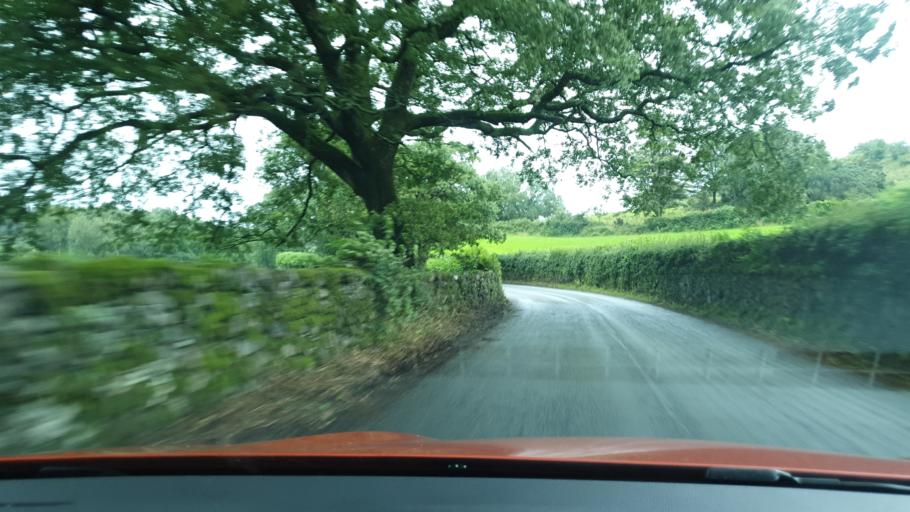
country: GB
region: England
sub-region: Cumbria
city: Seascale
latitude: 54.3978
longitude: -3.3477
